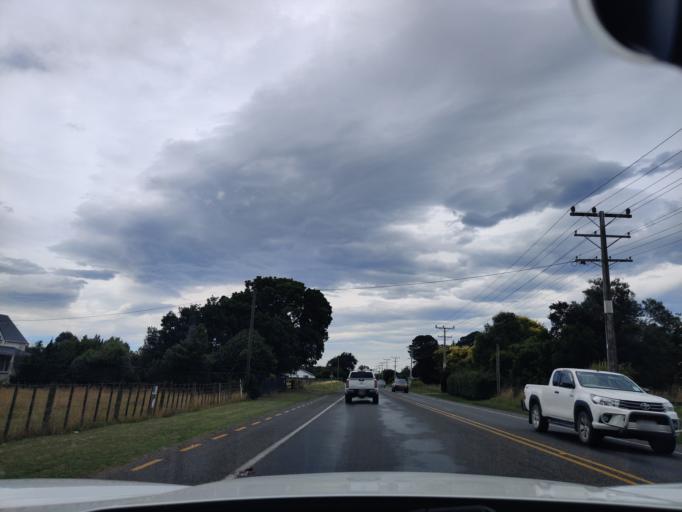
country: NZ
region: Wellington
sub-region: Masterton District
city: Masterton
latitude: -41.0099
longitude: 175.5491
